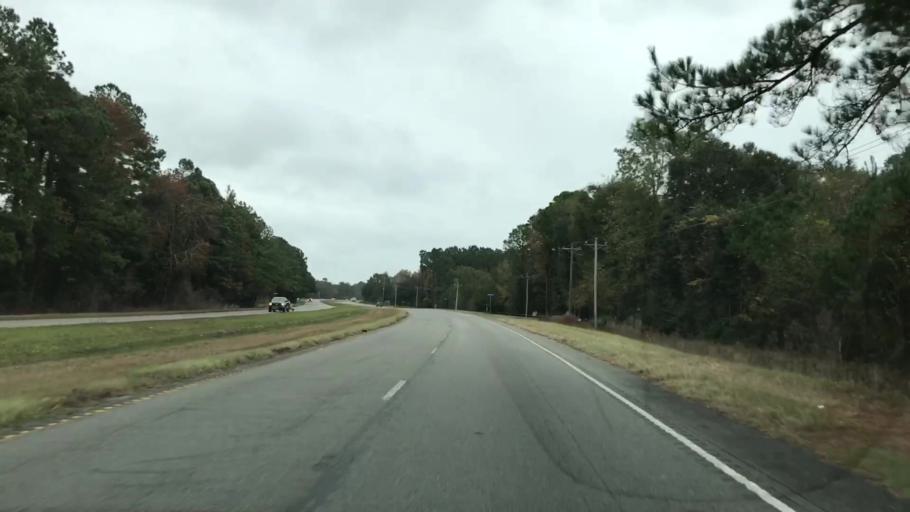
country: US
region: South Carolina
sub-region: Charleston County
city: Awendaw
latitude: 33.0400
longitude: -79.5925
